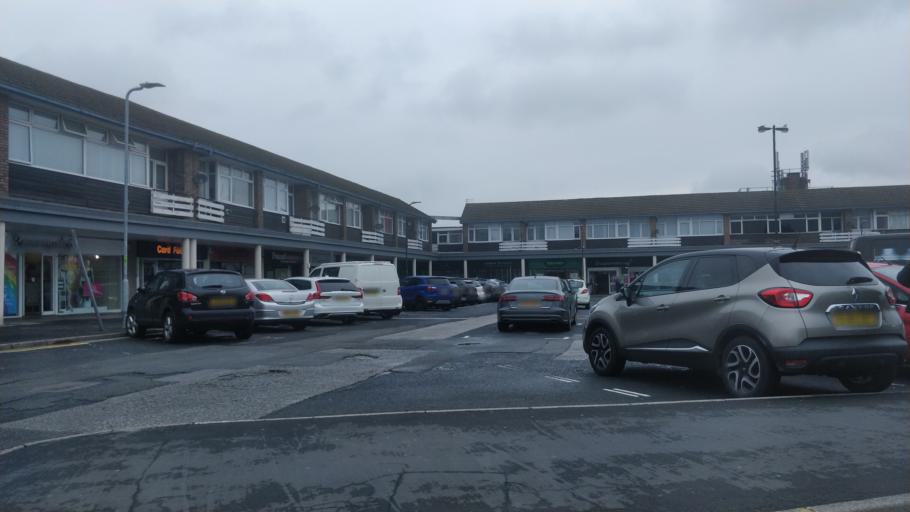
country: GB
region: England
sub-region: Sefton
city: Maghull
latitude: 53.5161
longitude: -2.9436
